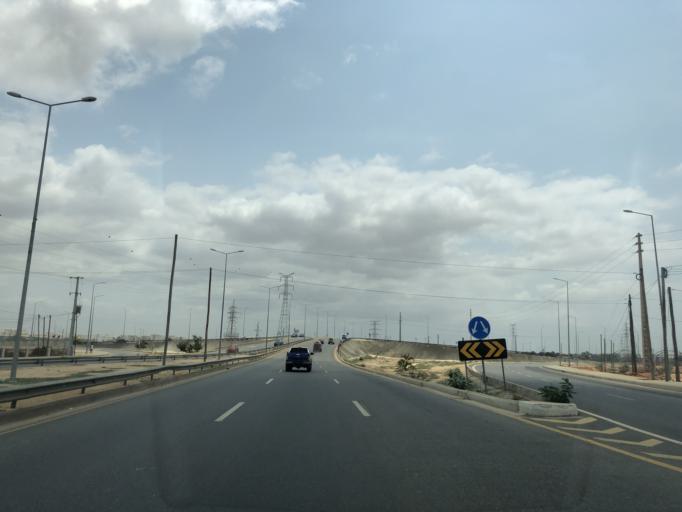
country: AO
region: Luanda
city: Luanda
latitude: -8.9702
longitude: 13.2546
